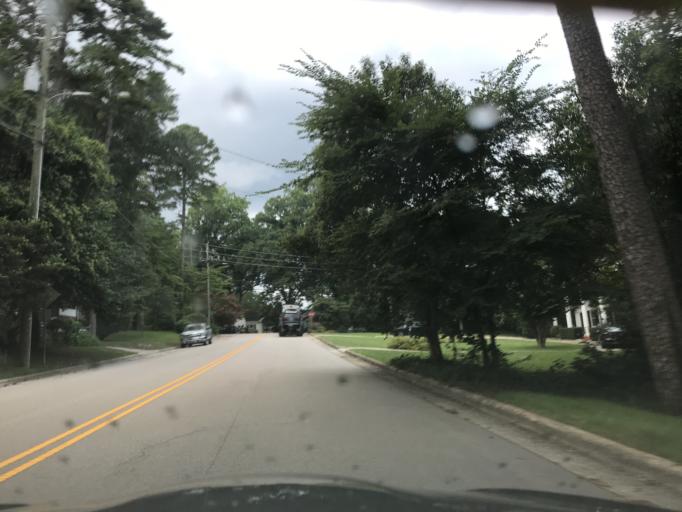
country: US
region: North Carolina
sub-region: Wake County
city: West Raleigh
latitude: 35.8114
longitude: -78.6657
